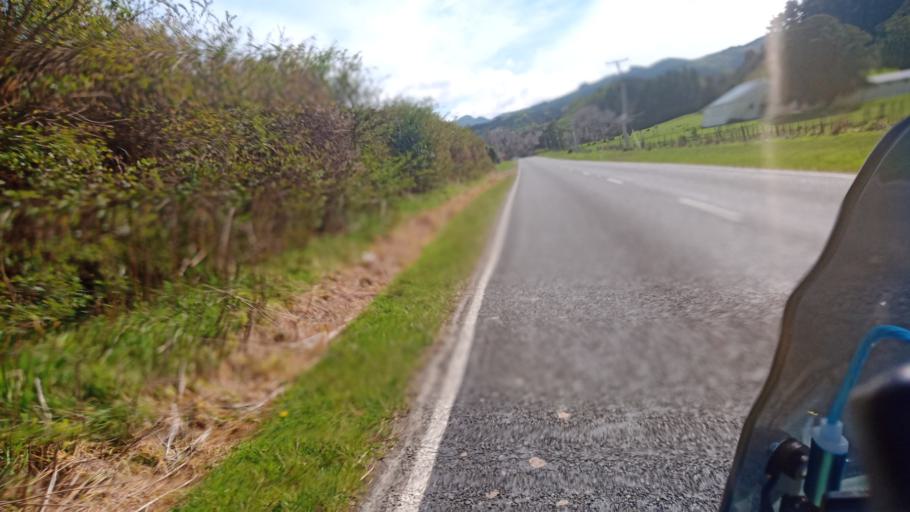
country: NZ
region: Gisborne
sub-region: Gisborne District
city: Gisborne
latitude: -37.8710
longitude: 178.2742
